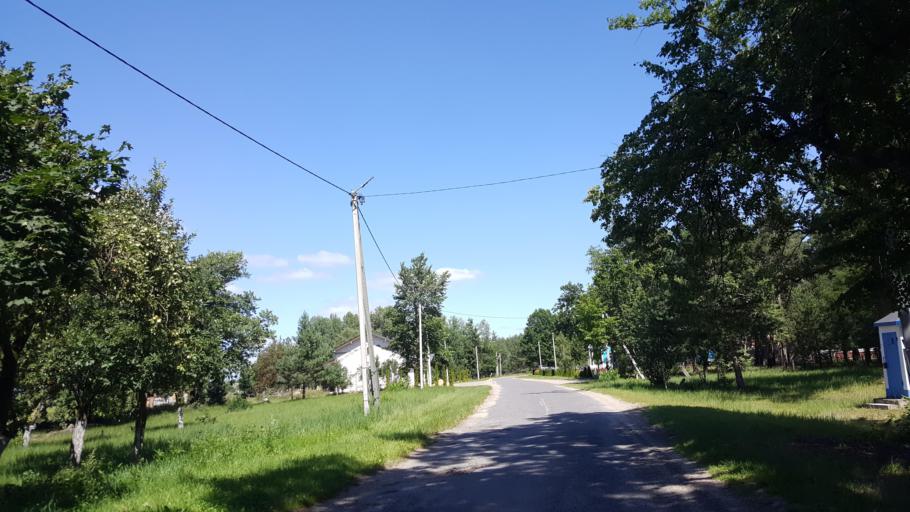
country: BY
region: Brest
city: Horad Kobryn
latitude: 52.3473
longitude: 24.3475
